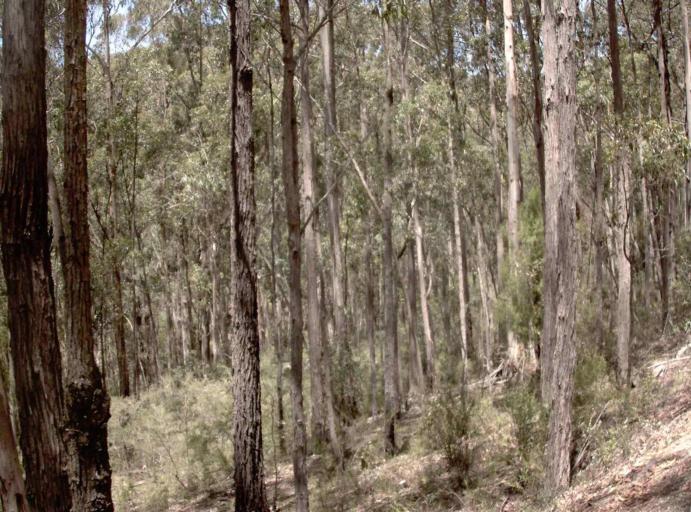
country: AU
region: Victoria
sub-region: East Gippsland
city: Lakes Entrance
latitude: -37.6009
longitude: 147.8881
